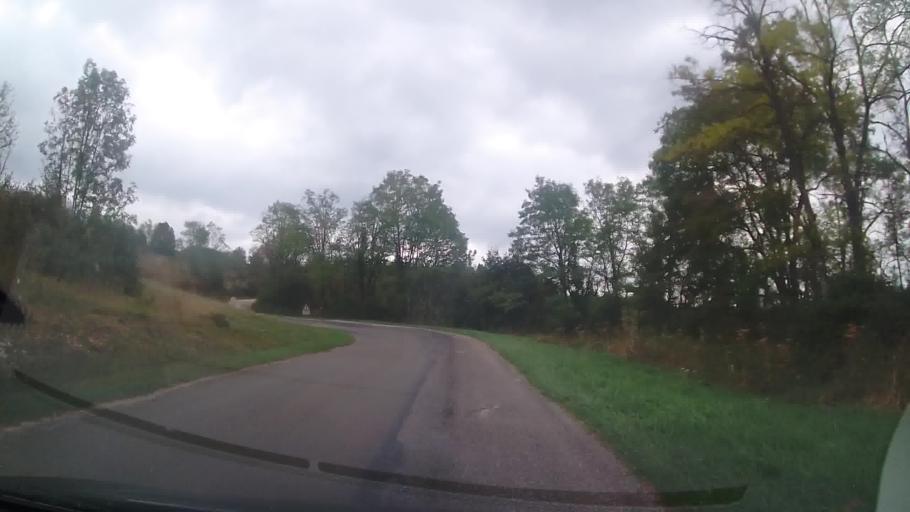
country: FR
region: Franche-Comte
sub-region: Departement du Jura
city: Arinthod
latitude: 46.3908
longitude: 5.5780
